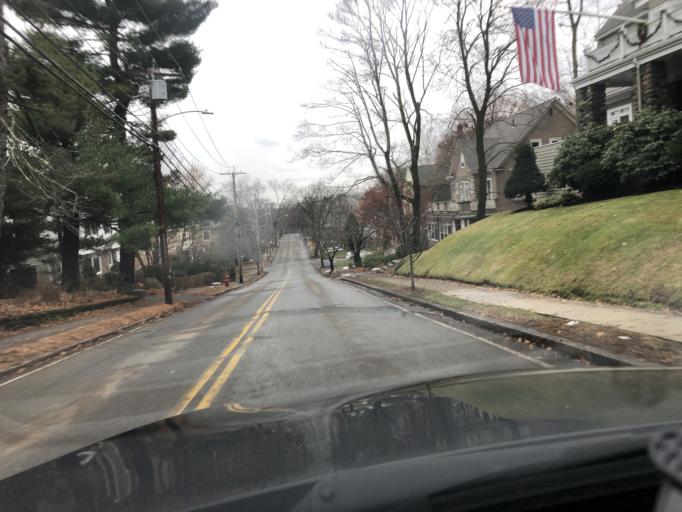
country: US
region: Massachusetts
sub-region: Middlesex County
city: Arlington
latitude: 42.4127
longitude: -71.1636
